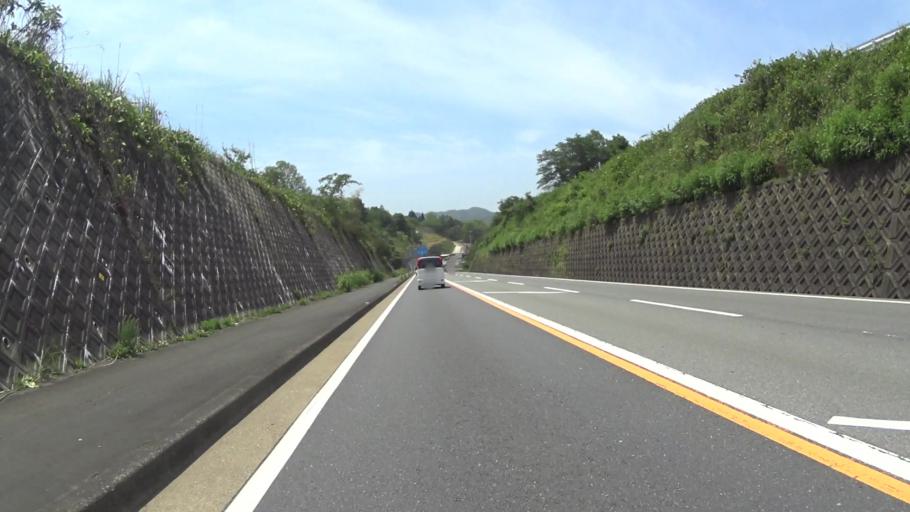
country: JP
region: Kyoto
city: Ayabe
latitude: 35.2198
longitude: 135.2303
